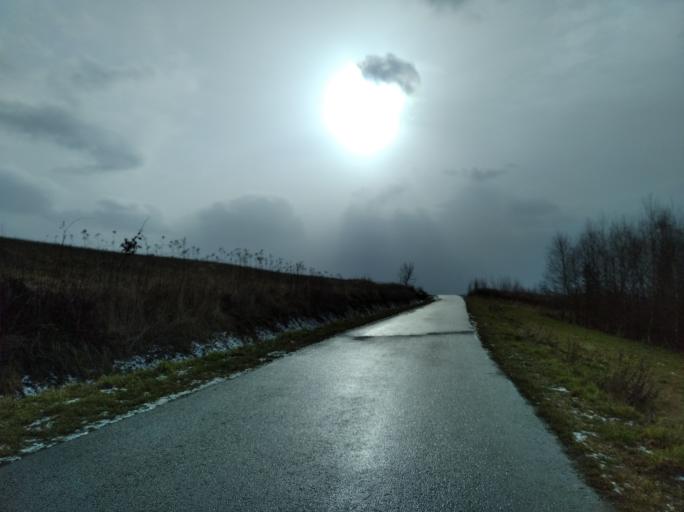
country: PL
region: Subcarpathian Voivodeship
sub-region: Powiat strzyzowski
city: Wysoka Strzyzowska
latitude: 49.8843
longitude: 21.7280
